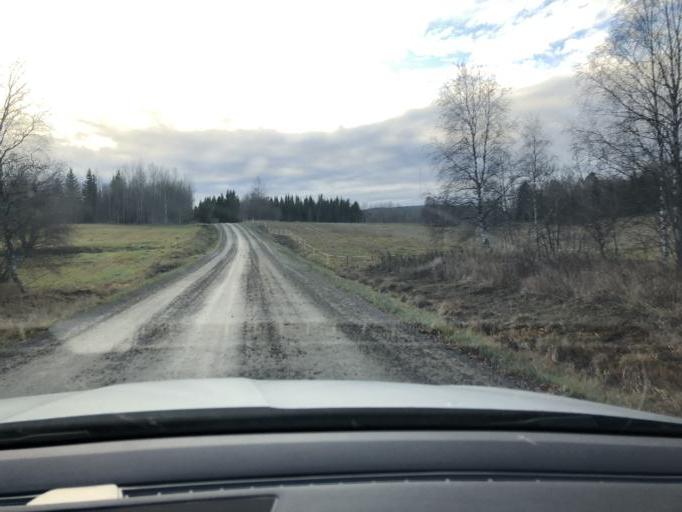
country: SE
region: Gaevleborg
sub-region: Hudiksvalls Kommun
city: Sorforsa
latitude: 61.7285
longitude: 16.9214
